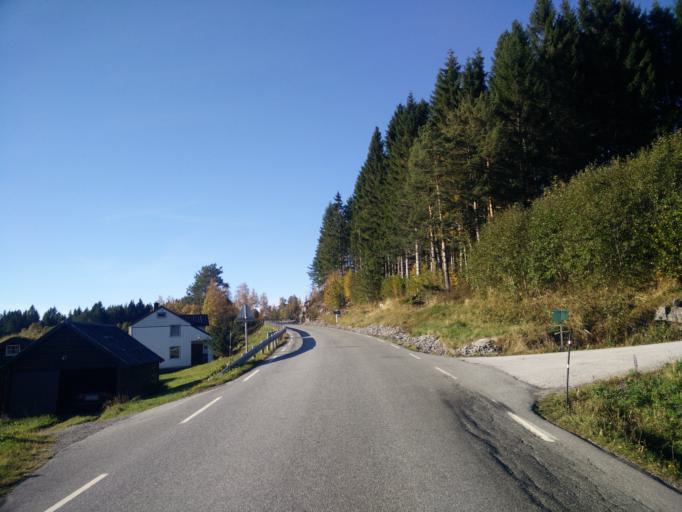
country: NO
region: More og Romsdal
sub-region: Halsa
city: Liaboen
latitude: 63.1168
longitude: 8.3142
